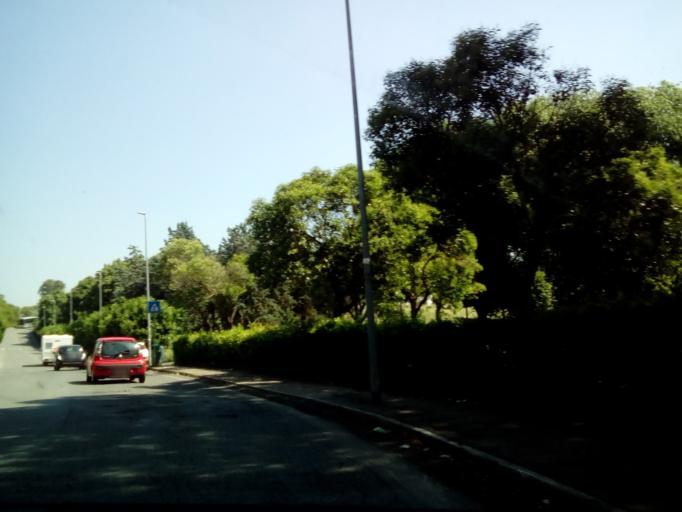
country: IT
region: Latium
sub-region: Citta metropolitana di Roma Capitale
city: Rome
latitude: 41.8899
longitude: 12.5806
